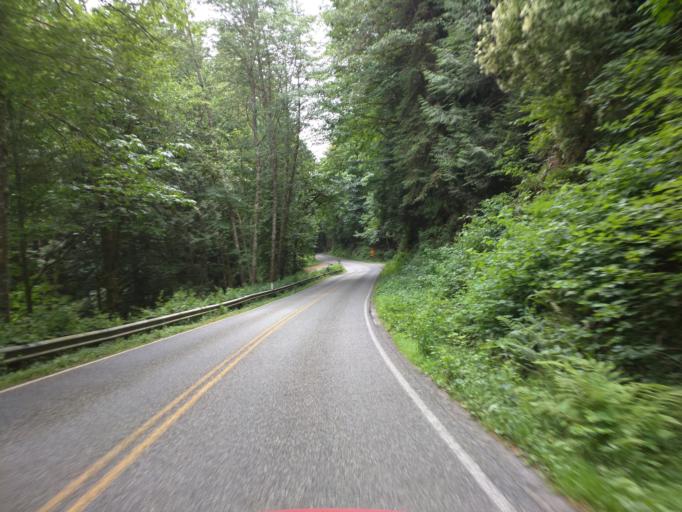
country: US
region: Washington
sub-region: Whatcom County
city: Sudden Valley
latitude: 48.6991
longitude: -122.3147
